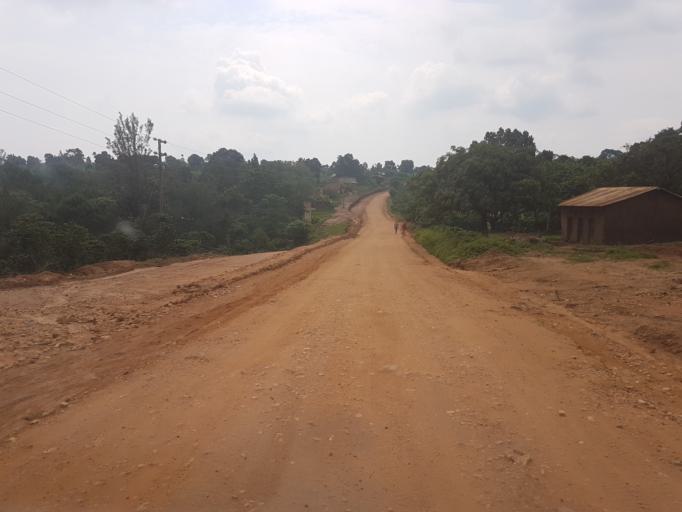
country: UG
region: Western Region
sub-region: Kanungu District
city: Ntungamo
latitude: -0.8189
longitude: 29.7073
